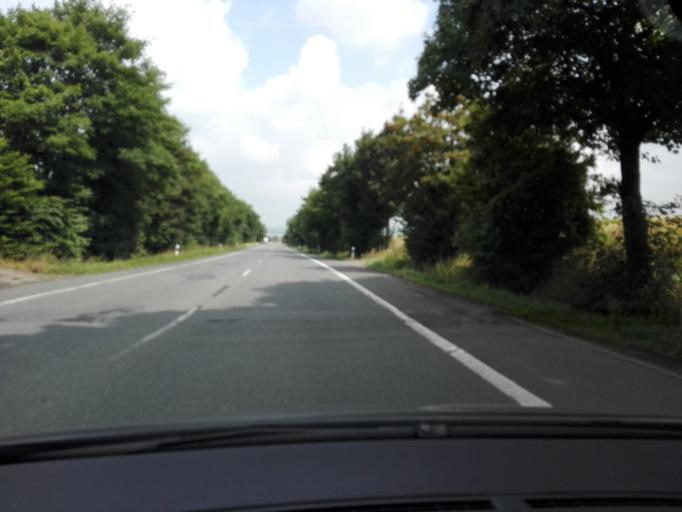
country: DE
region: North Rhine-Westphalia
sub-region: Regierungsbezirk Arnsberg
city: Frondenberg
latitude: 51.5266
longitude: 7.7701
